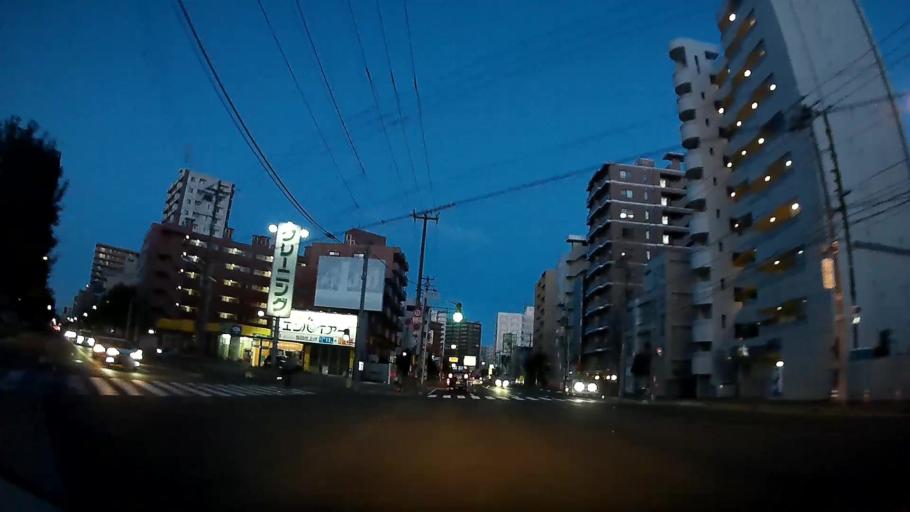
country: JP
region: Hokkaido
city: Sapporo
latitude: 43.0643
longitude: 141.3156
